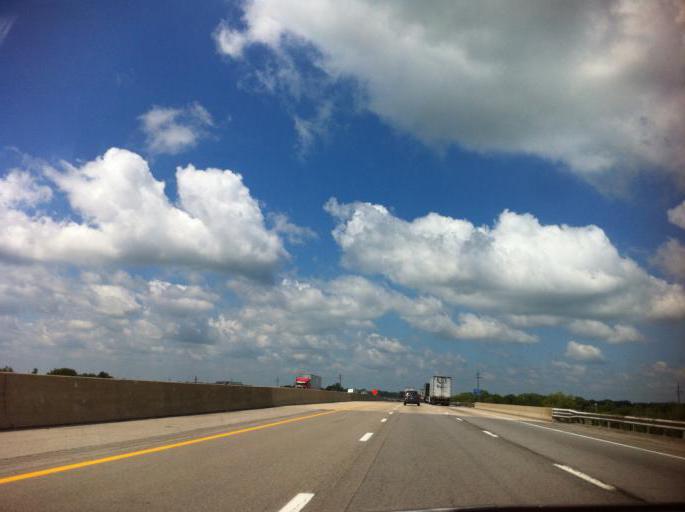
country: US
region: Ohio
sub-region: Huron County
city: Bellevue
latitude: 41.3448
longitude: -82.7856
